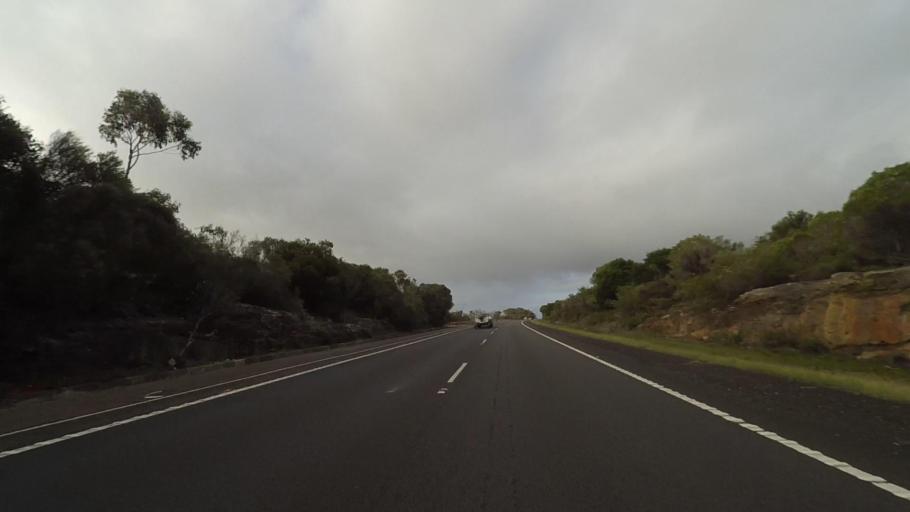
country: AU
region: New South Wales
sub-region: Wollongong
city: Bulli
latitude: -34.2638
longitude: 150.9277
